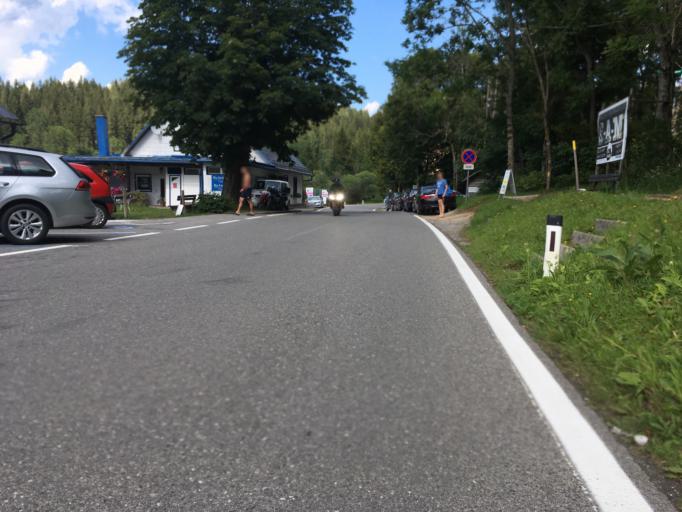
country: AT
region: Lower Austria
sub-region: Politischer Bezirk Lilienfeld
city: Mitterbach am Erlaufsee
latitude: 47.7899
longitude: 15.2800
